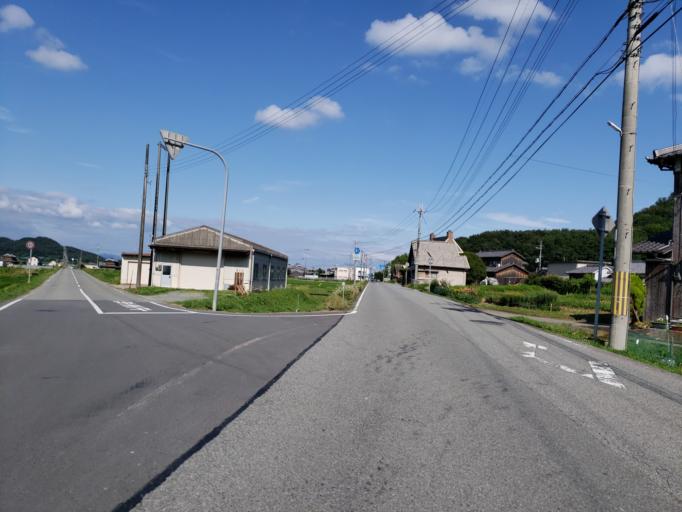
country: JP
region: Hyogo
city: Kakogawacho-honmachi
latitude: 34.8954
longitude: 134.8041
